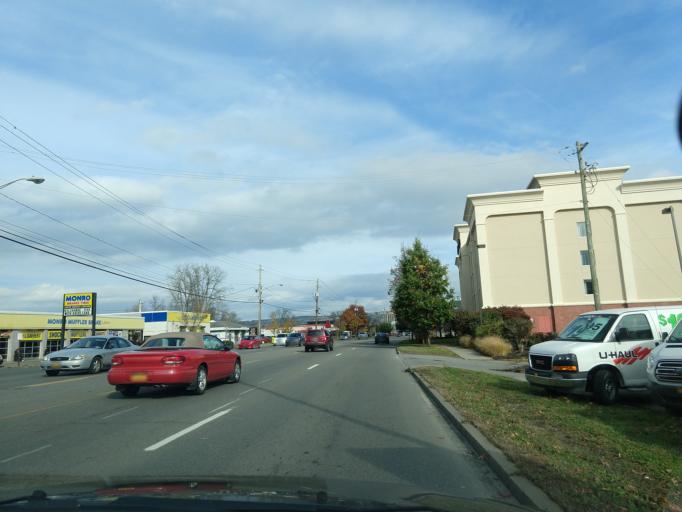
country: US
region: New York
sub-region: Tompkins County
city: South Hill
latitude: 42.4245
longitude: -76.5140
